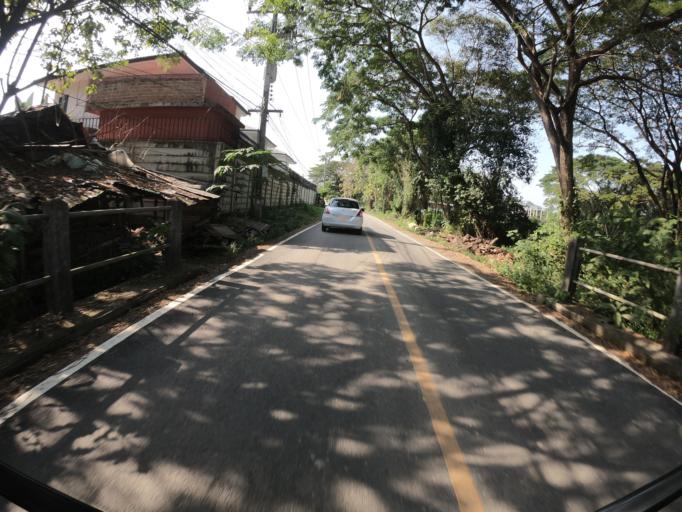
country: TH
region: Chiang Mai
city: San Sai
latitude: 18.8449
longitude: 99.0032
